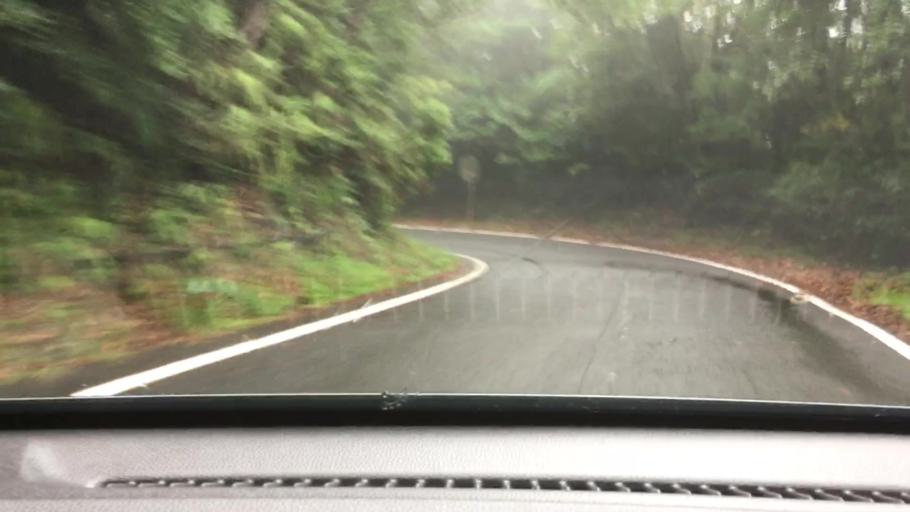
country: JP
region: Nagasaki
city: Togitsu
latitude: 32.9163
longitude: 129.7335
